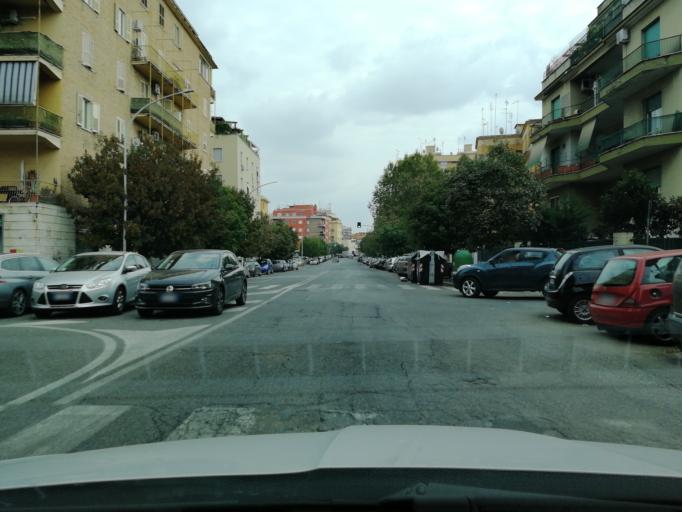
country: IT
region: Latium
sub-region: Citta metropolitana di Roma Capitale
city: Rome
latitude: 41.8619
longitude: 12.5472
